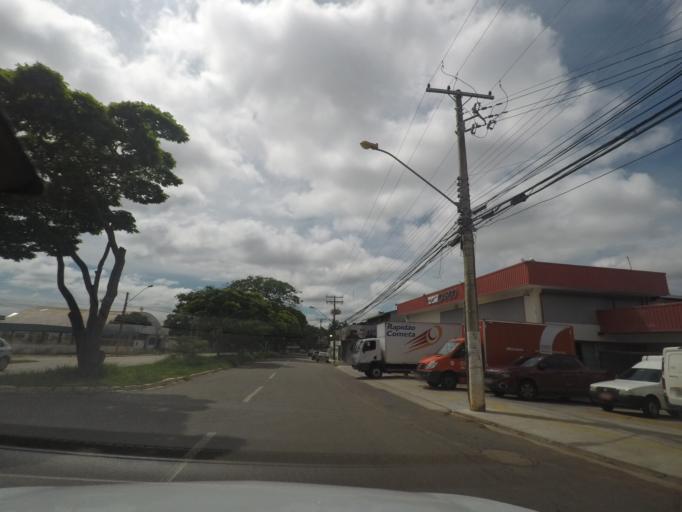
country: BR
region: Goias
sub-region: Goiania
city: Goiania
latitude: -16.6338
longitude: -49.2269
